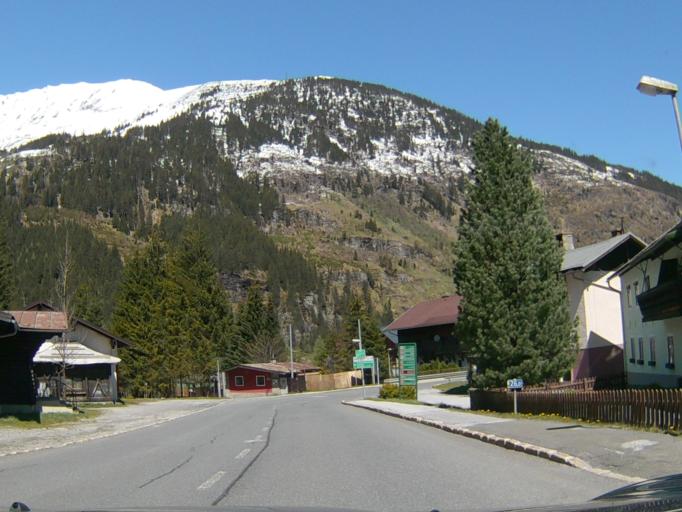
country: AT
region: Salzburg
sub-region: Politischer Bezirk Sankt Johann im Pongau
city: Bad Gastein
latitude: 47.0867
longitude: 13.1200
